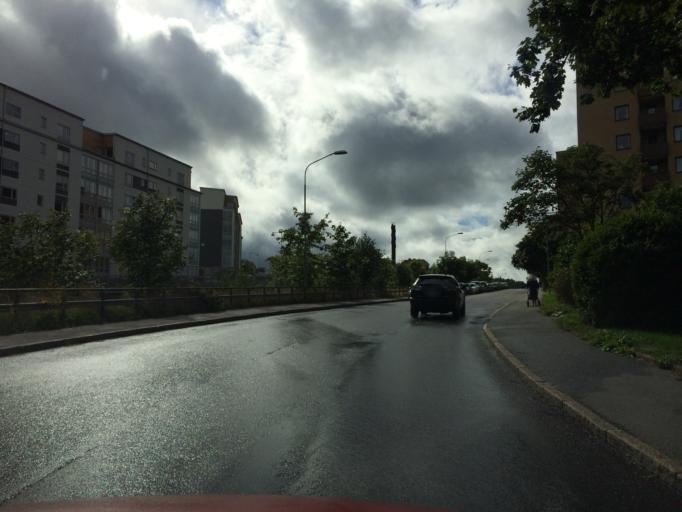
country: SE
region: Stockholm
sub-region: Stockholms Kommun
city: Bromma
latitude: 59.3049
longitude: 17.9803
